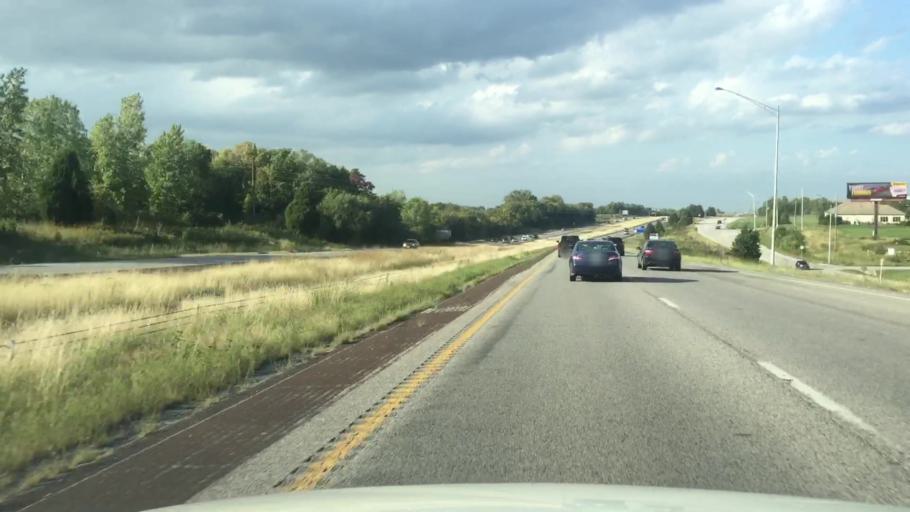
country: US
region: Missouri
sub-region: Jackson County
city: Lees Summit
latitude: 38.9868
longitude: -94.3569
